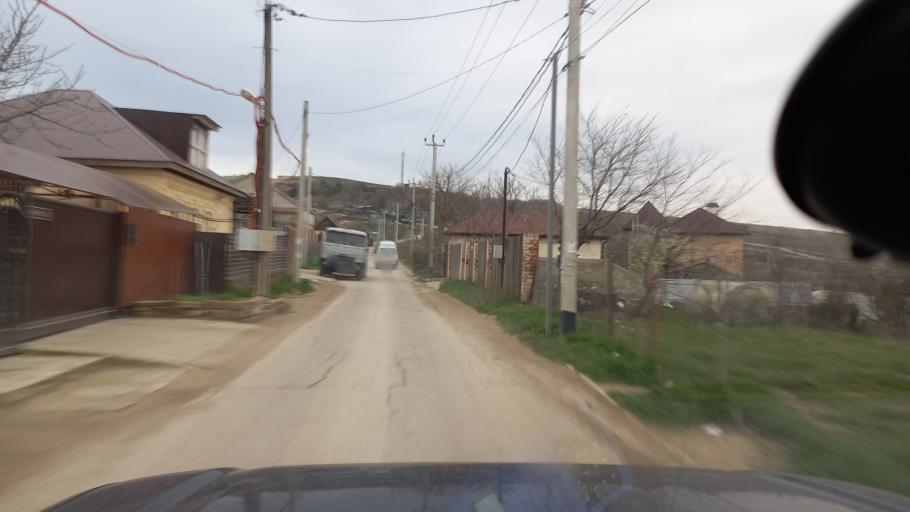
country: RU
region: Krasnodarskiy
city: Anapa
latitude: 44.8501
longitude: 37.3487
